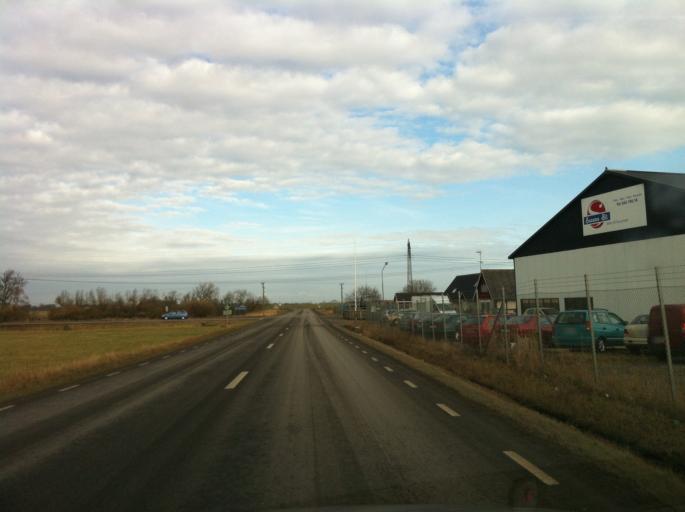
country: SE
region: Skane
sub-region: Bjuvs Kommun
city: Bjuv
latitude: 56.1021
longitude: 12.8935
